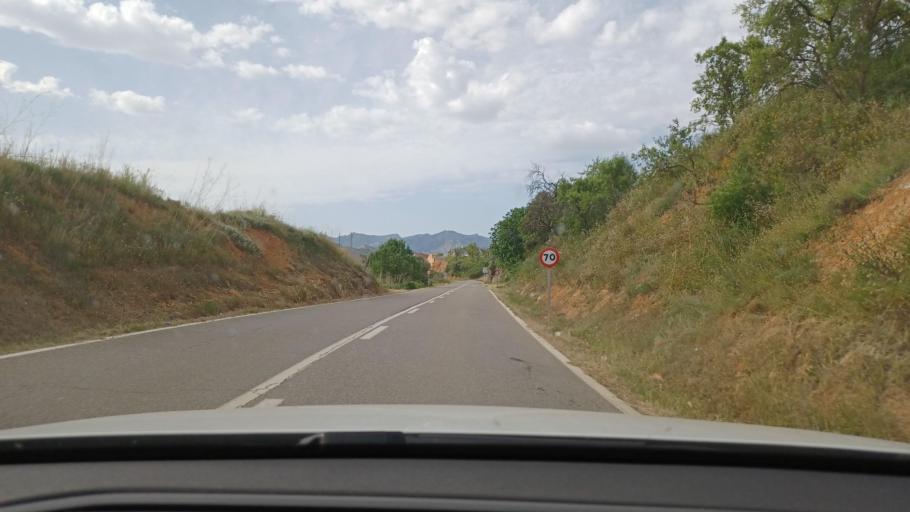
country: ES
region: Catalonia
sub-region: Provincia de Tarragona
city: Bot
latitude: 41.0146
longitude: 0.3855
